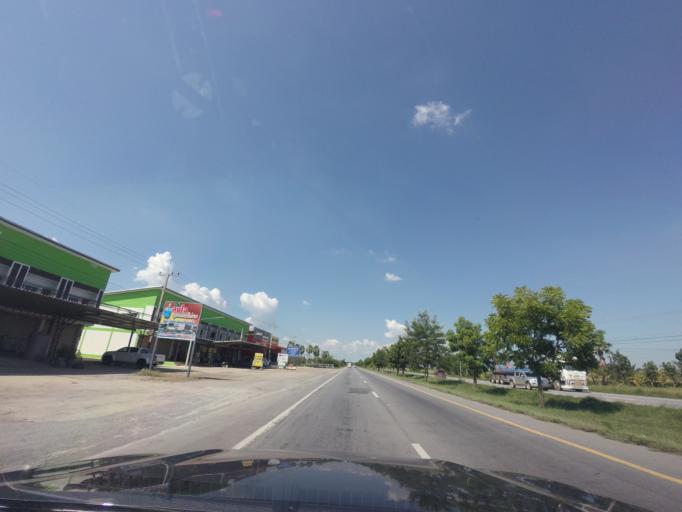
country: TH
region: Nakhon Ratchasima
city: Non Sung
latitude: 15.1753
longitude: 102.3366
